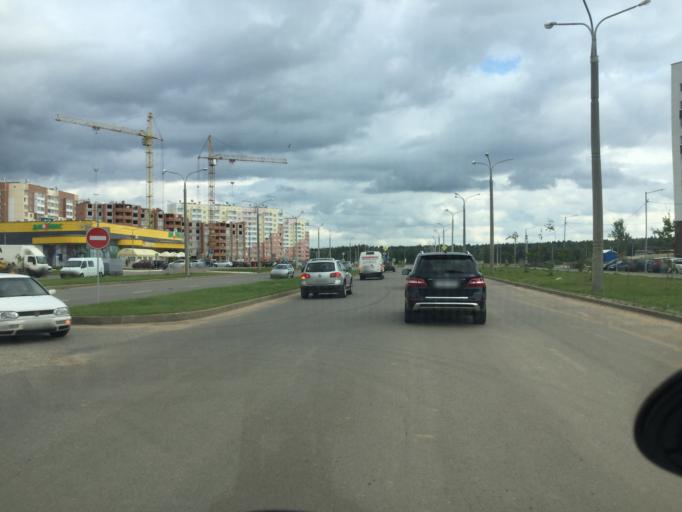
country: BY
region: Vitebsk
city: Vitebsk
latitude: 55.1641
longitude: 30.2733
